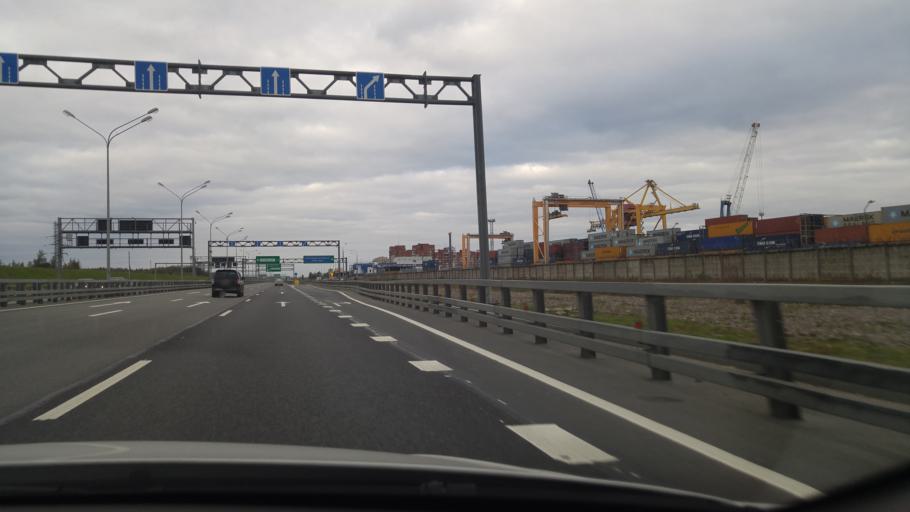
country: RU
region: St.-Petersburg
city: Kronshtadt
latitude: 60.0033
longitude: 29.7059
